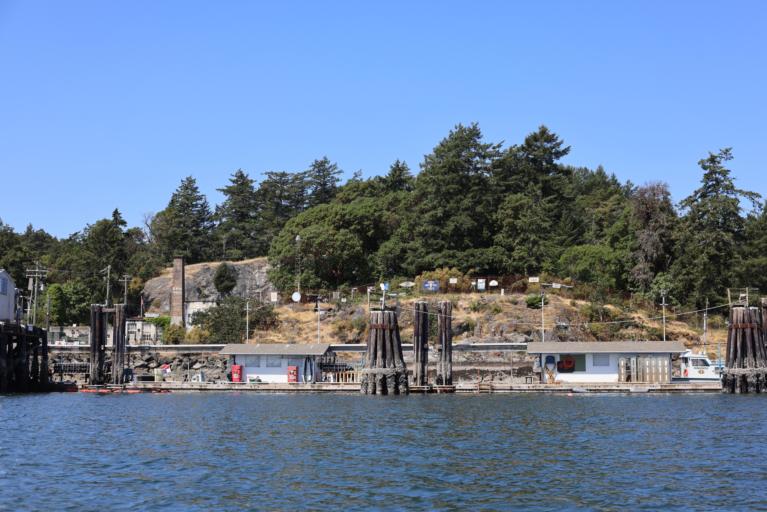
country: CA
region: British Columbia
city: Colwood
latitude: 48.4447
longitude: -123.4481
